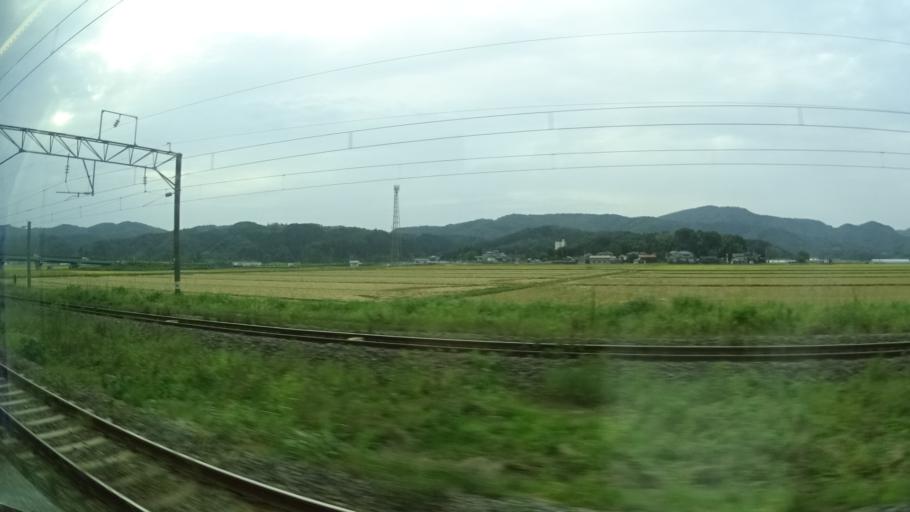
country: JP
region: Yamagata
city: Tsuruoka
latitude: 38.7133
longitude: 139.7313
